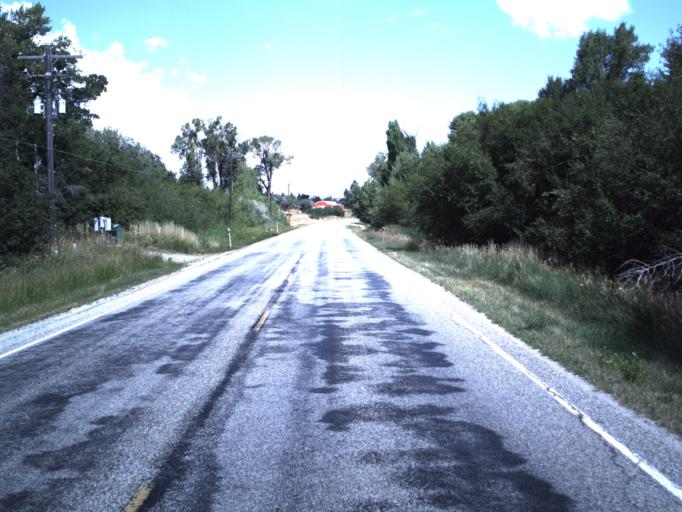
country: US
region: Idaho
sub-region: Bear Lake County
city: Paris
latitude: 41.9904
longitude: -111.4113
